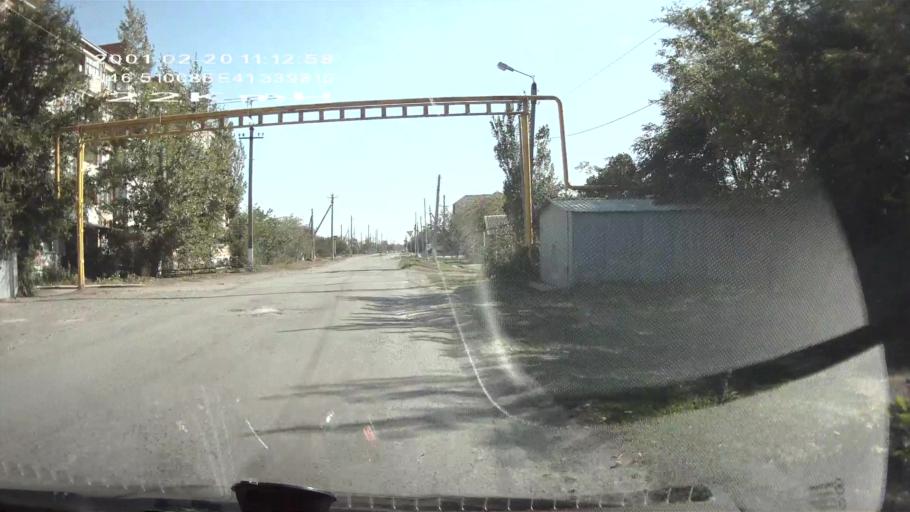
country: RU
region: Rostov
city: Gigant
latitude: 46.5101
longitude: 41.3401
